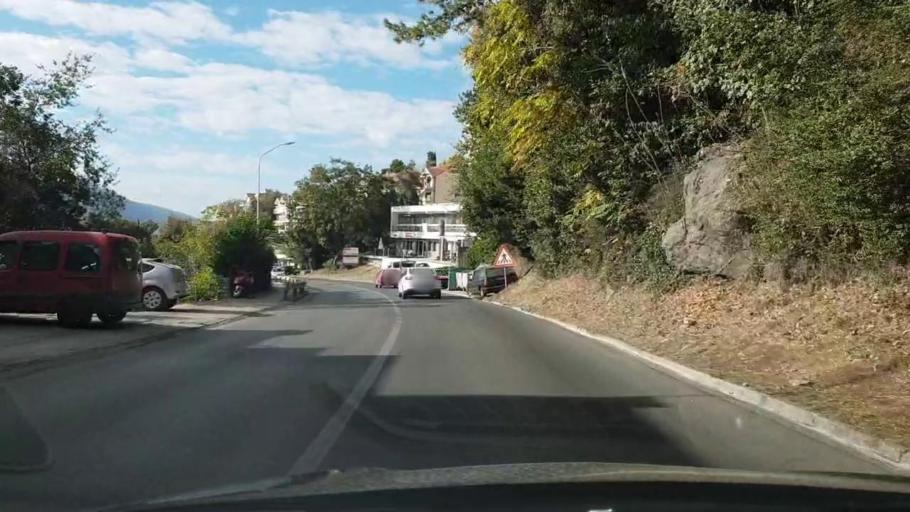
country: ME
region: Herceg Novi
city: Herceg-Novi
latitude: 42.4546
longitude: 18.5314
